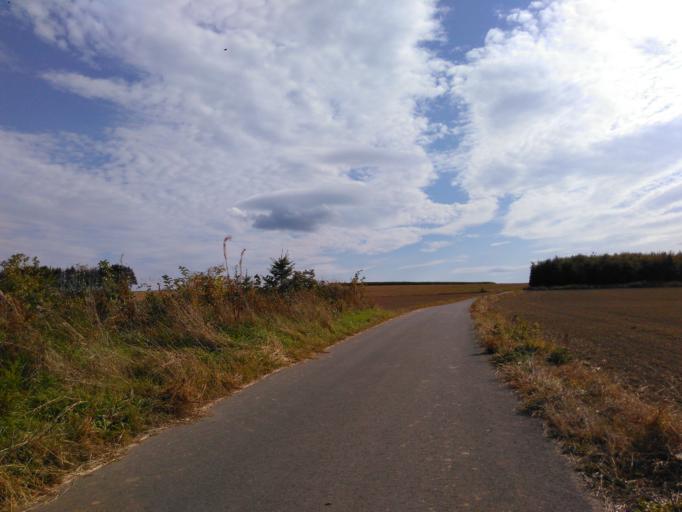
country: BE
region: Wallonia
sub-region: Province du Luxembourg
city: Gouvy
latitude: 50.1715
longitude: 5.9642
